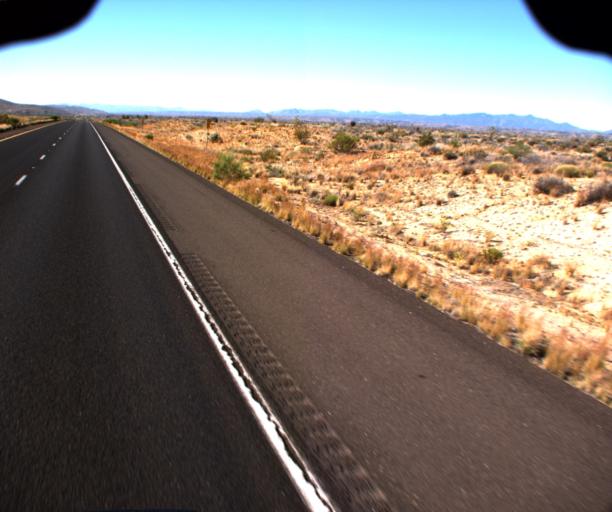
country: US
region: Arizona
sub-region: Mohave County
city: Kingman
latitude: 35.0714
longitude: -113.6659
